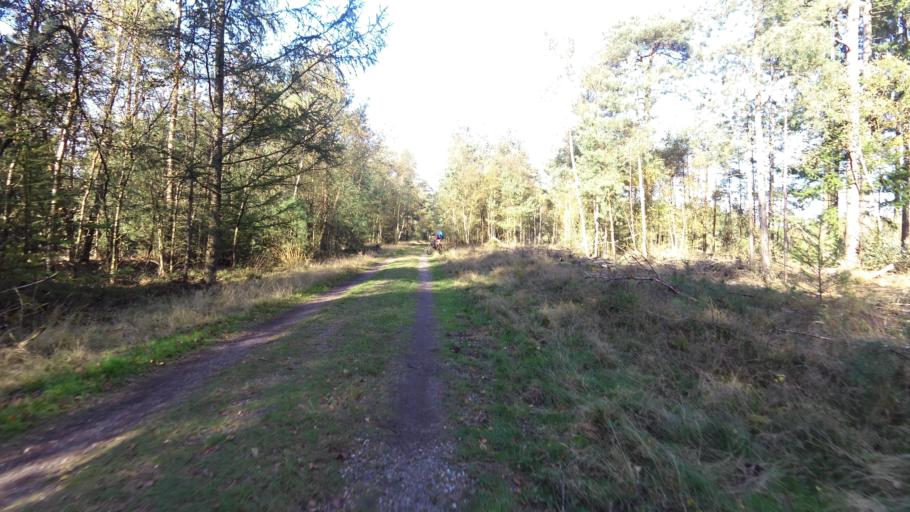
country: NL
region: Gelderland
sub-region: Gemeente Epe
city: Epe
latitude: 52.3759
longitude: 5.9519
